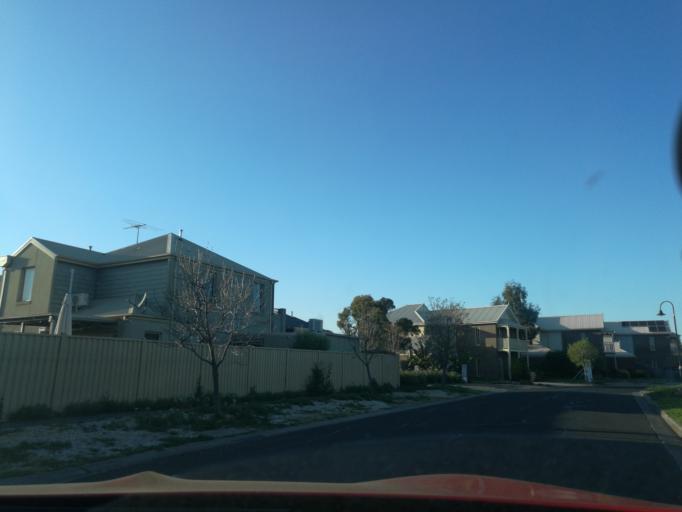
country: AU
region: Victoria
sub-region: Wyndham
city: Williams Landing
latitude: -37.8786
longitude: 144.7449
